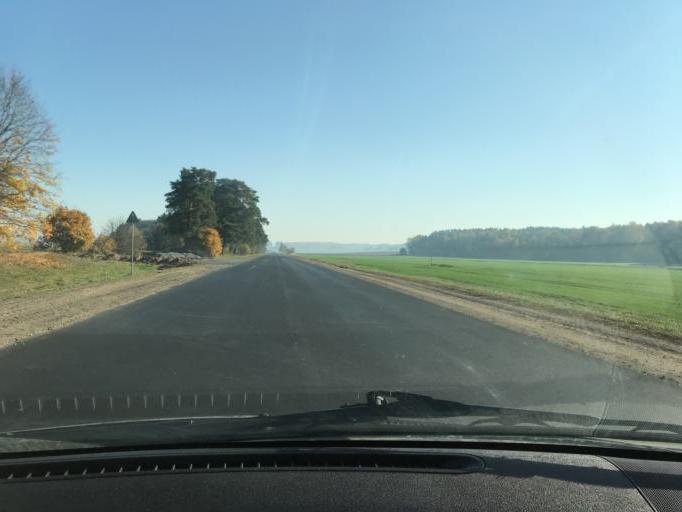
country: BY
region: Minsk
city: Klyetsk
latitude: 52.9675
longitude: 26.5786
